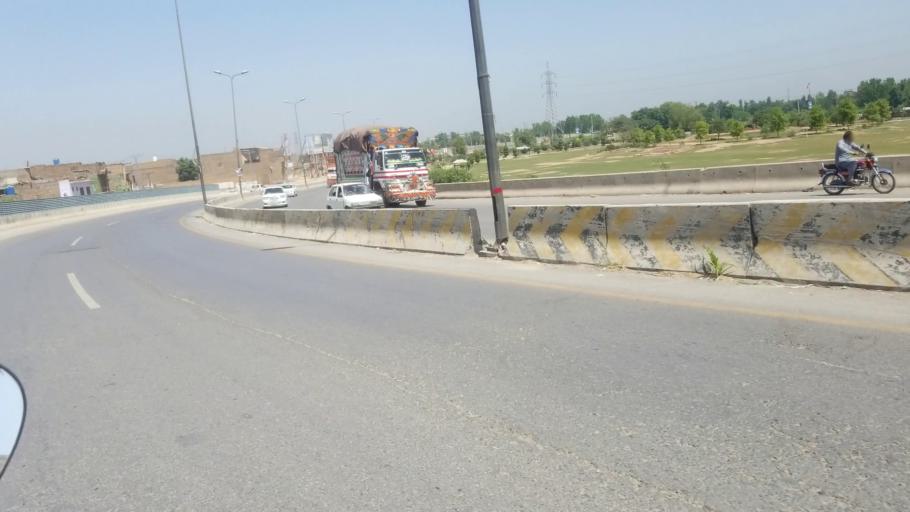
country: PK
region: Khyber Pakhtunkhwa
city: Peshawar
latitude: 34.0245
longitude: 71.6173
